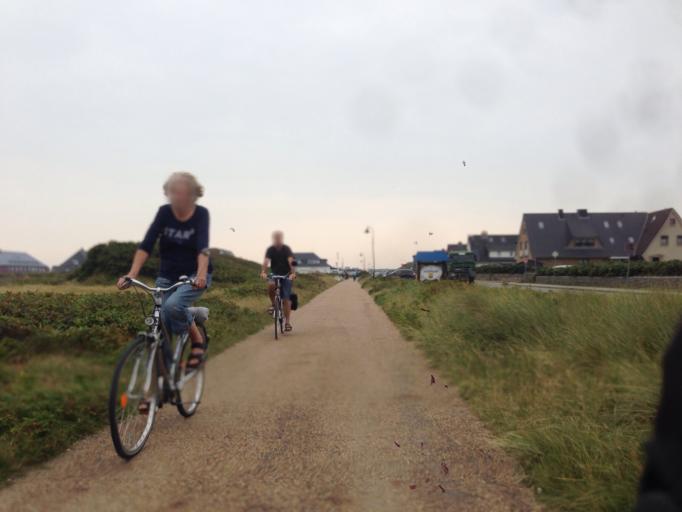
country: DE
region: Schleswig-Holstein
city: Norddorf
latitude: 54.7723
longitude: 8.2862
